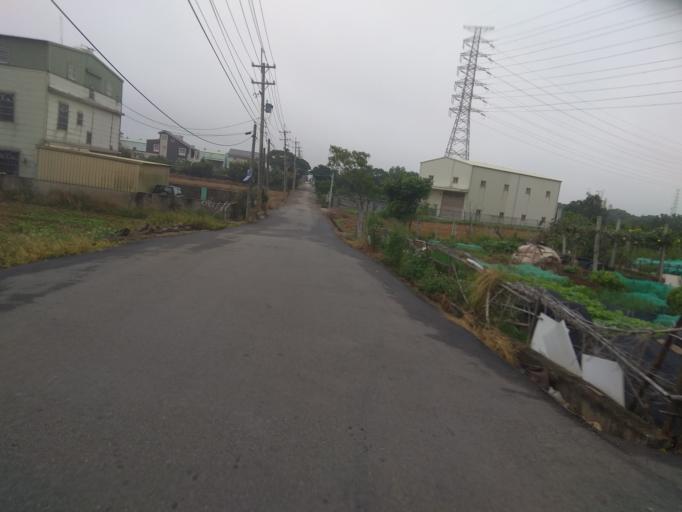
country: TW
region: Taiwan
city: Taoyuan City
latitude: 24.9921
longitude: 121.1260
